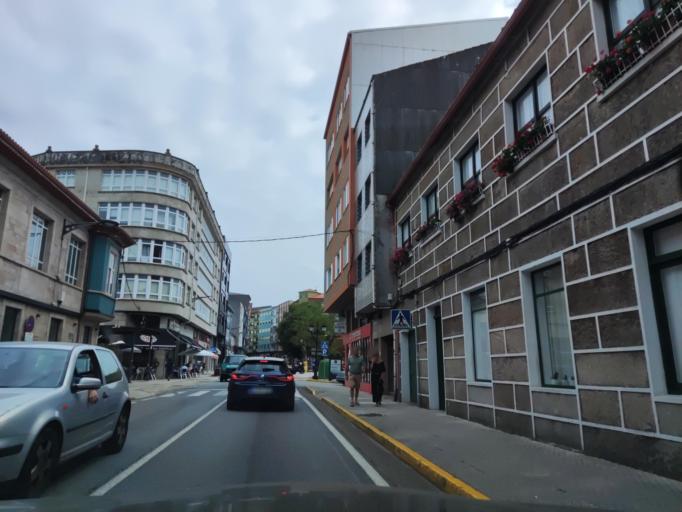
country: ES
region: Galicia
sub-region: Provincia da Coruna
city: Boiro
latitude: 42.6474
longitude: -8.8838
